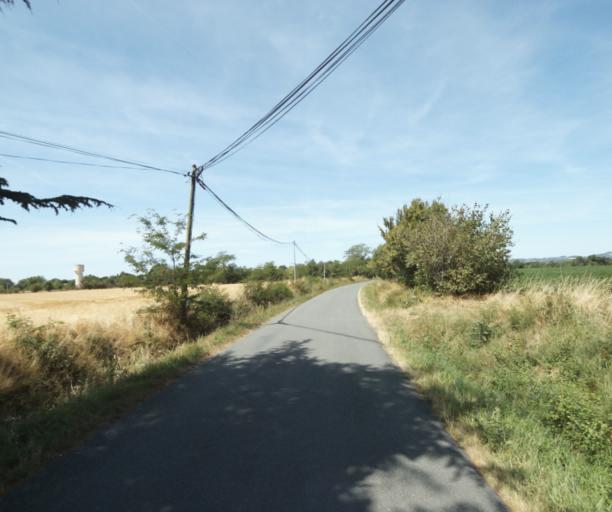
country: FR
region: Midi-Pyrenees
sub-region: Departement de la Haute-Garonne
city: Revel
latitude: 43.4977
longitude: 2.0030
